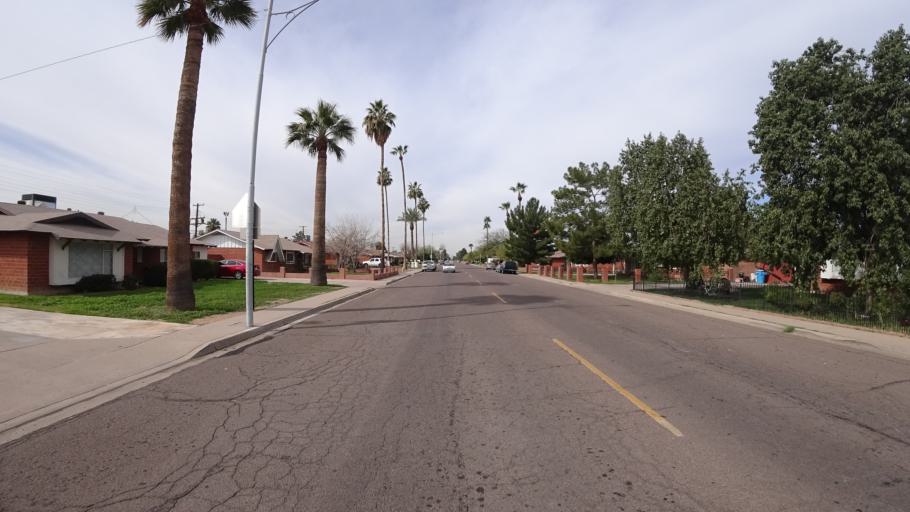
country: US
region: Arizona
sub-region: Maricopa County
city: Glendale
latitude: 33.5312
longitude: -112.1444
